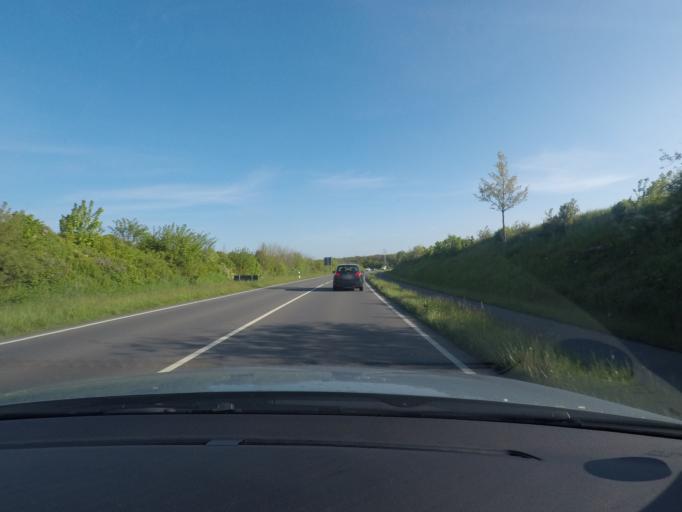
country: DE
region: Lower Saxony
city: Wolsdorf
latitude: 52.1965
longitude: 10.9679
